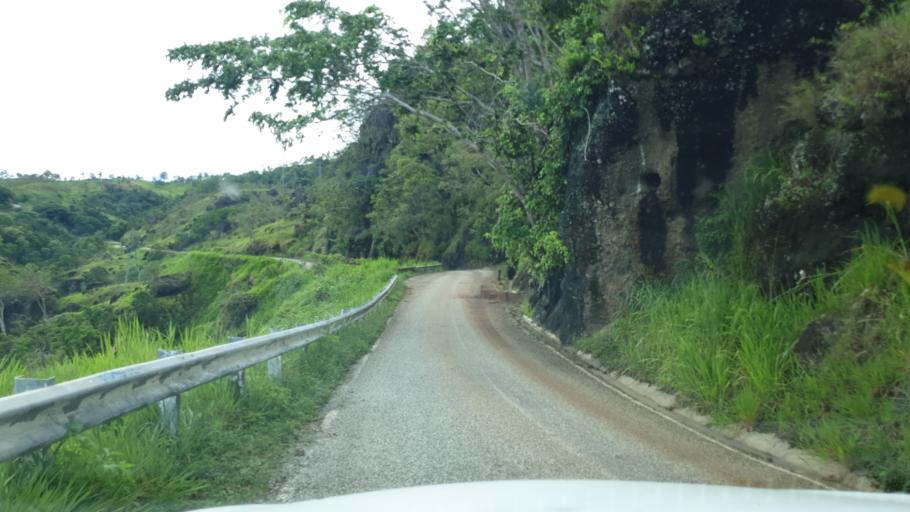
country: PG
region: National Capital
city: Port Moresby
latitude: -9.4238
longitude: 147.3814
